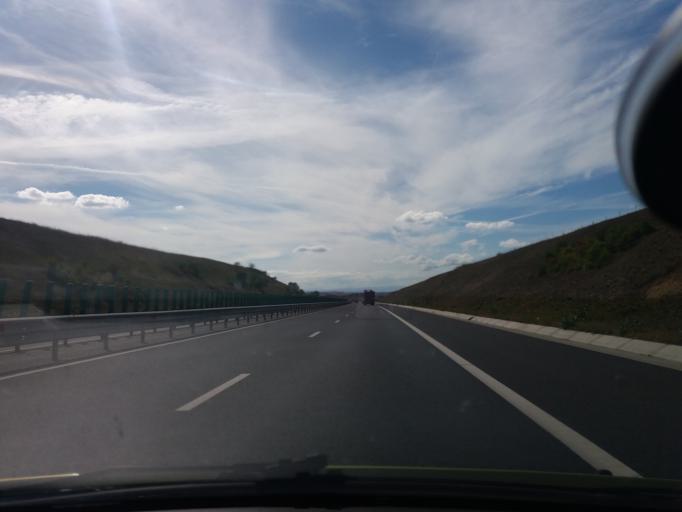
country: RO
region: Alba
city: Vurpar
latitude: 45.9586
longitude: 23.4436
